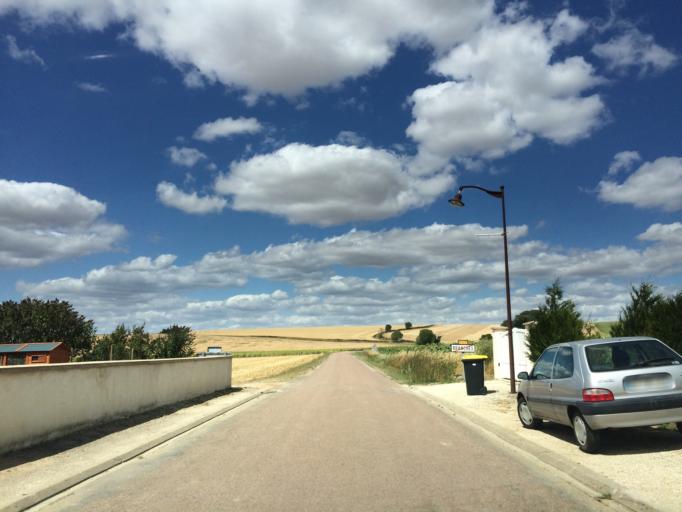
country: FR
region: Bourgogne
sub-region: Departement de l'Yonne
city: Fleury-la-Vallee
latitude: 47.8892
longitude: 3.4814
